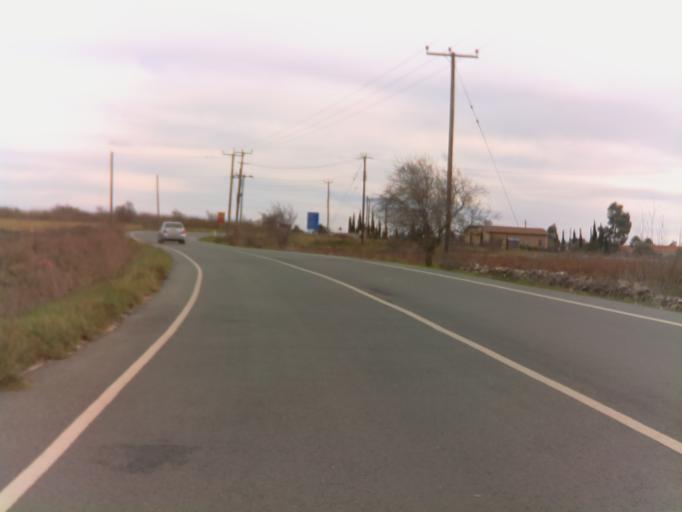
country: CY
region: Pafos
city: Pegeia
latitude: 34.9258
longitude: 32.4185
